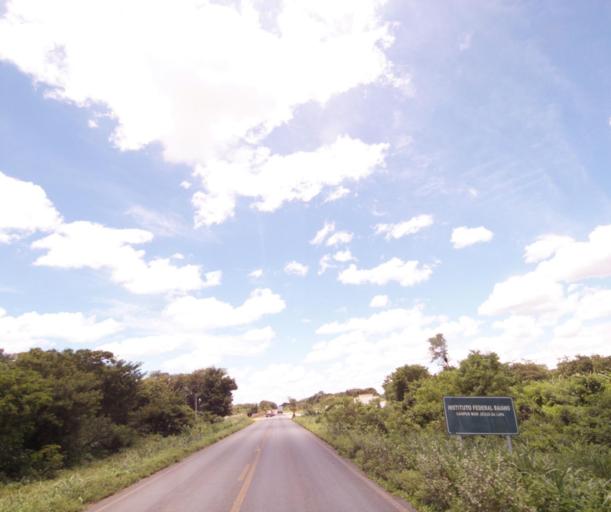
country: BR
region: Bahia
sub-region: Bom Jesus Da Lapa
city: Bom Jesus da Lapa
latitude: -13.2629
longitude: -43.5454
